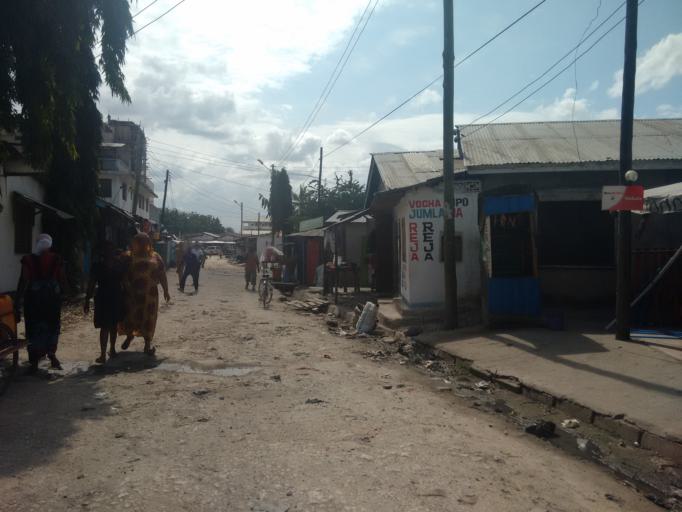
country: TZ
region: Dar es Salaam
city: Dar es Salaam
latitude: -6.8441
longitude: 39.2677
